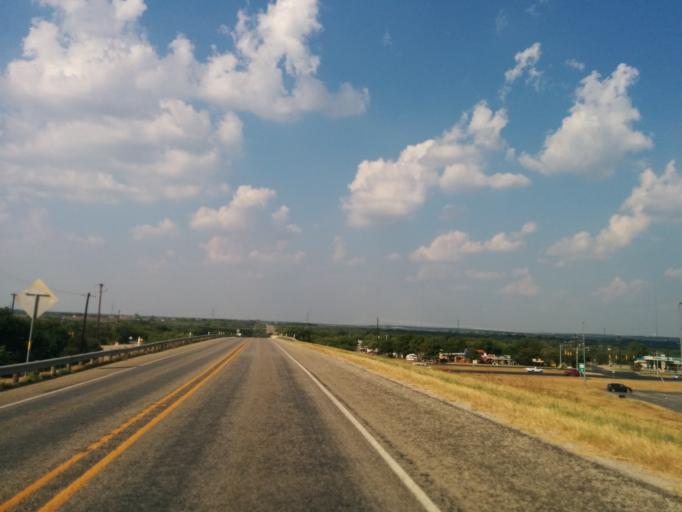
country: US
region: Texas
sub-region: Bexar County
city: Elmendorf
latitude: 29.2661
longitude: -98.3077
